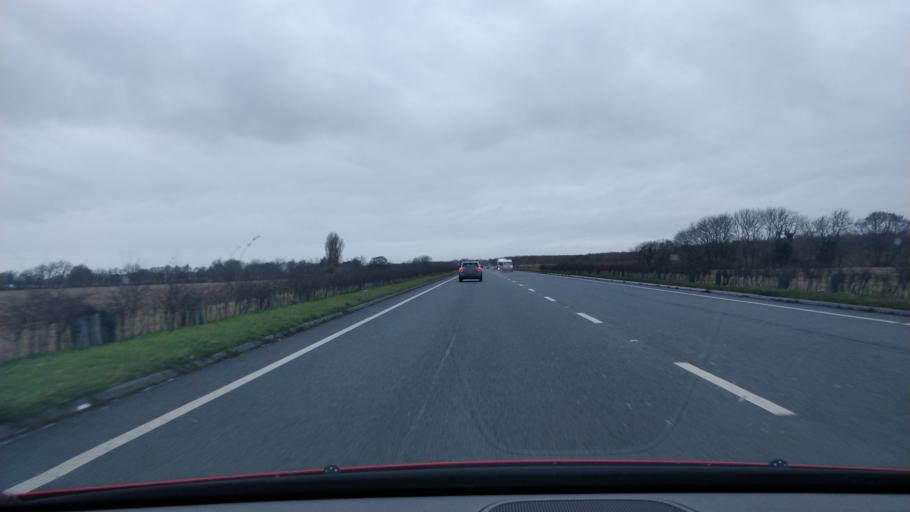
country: GB
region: England
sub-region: Sefton
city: Thornton
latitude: 53.4993
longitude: -2.9842
